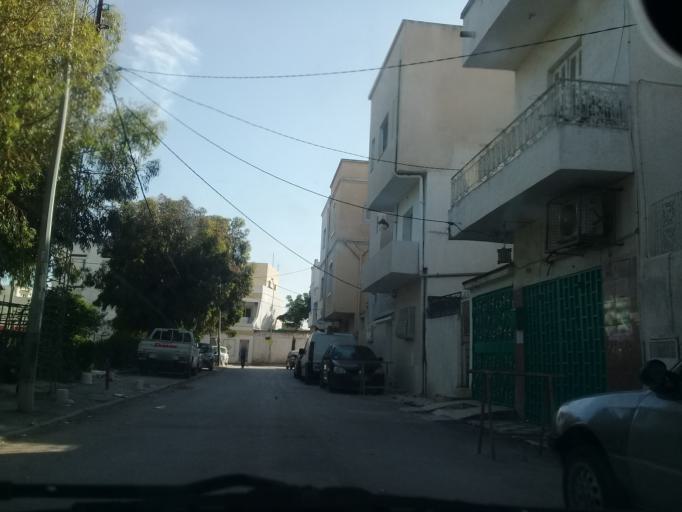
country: TN
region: Ariana
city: Ariana
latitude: 36.8306
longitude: 10.1939
